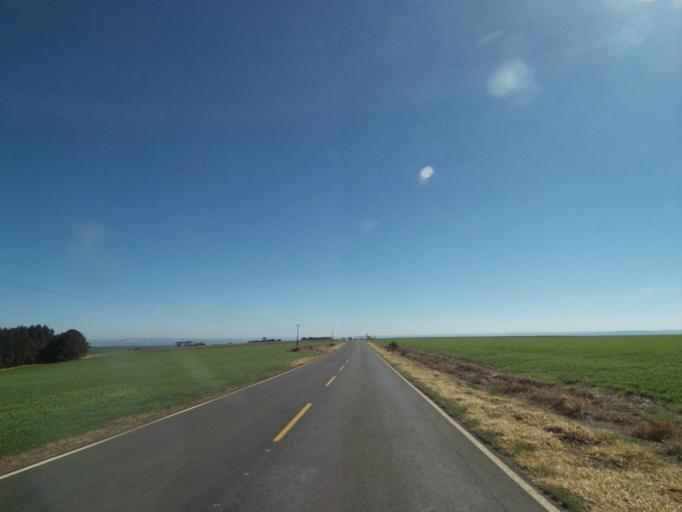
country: BR
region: Parana
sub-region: Tibagi
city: Tibagi
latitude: -24.5469
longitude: -50.2978
